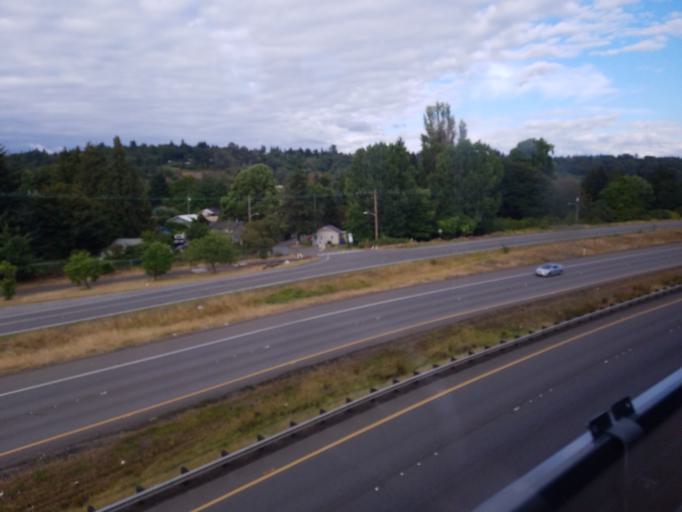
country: US
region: Washington
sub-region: King County
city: Riverton
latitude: 47.4966
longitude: -122.2848
